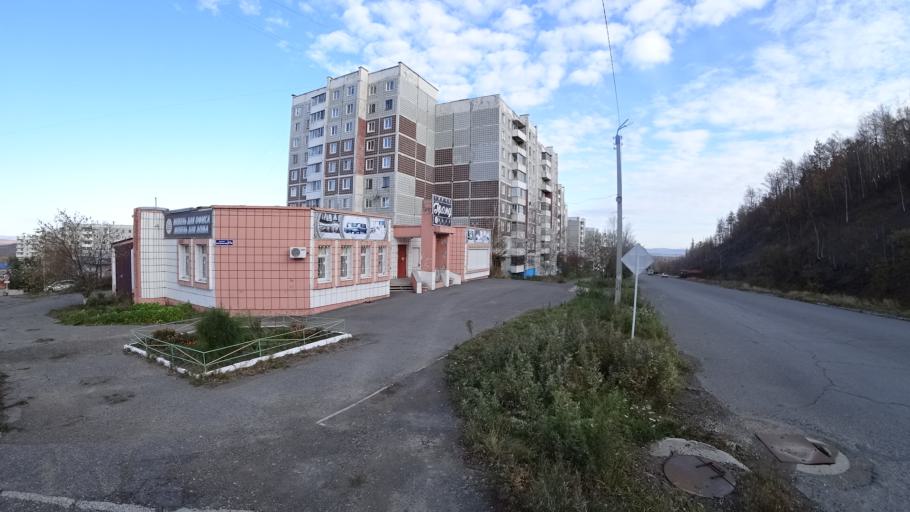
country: RU
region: Khabarovsk Krai
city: Amursk
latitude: 50.2458
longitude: 136.9215
